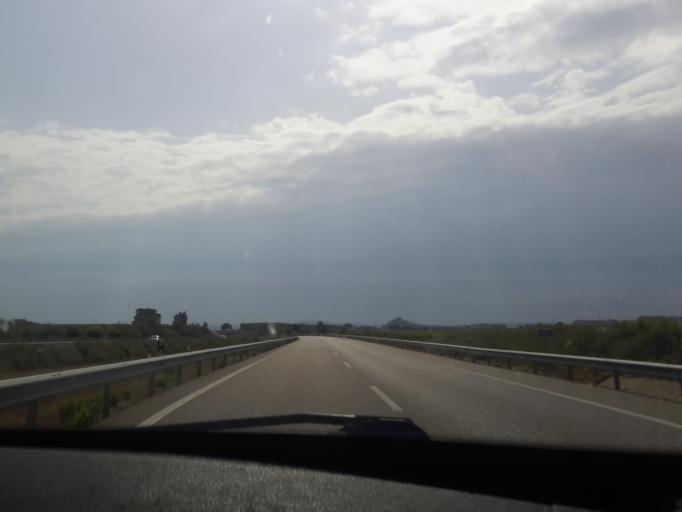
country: ES
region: Catalonia
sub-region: Provincia de Lleida
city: Seros
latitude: 41.5083
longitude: 0.4214
